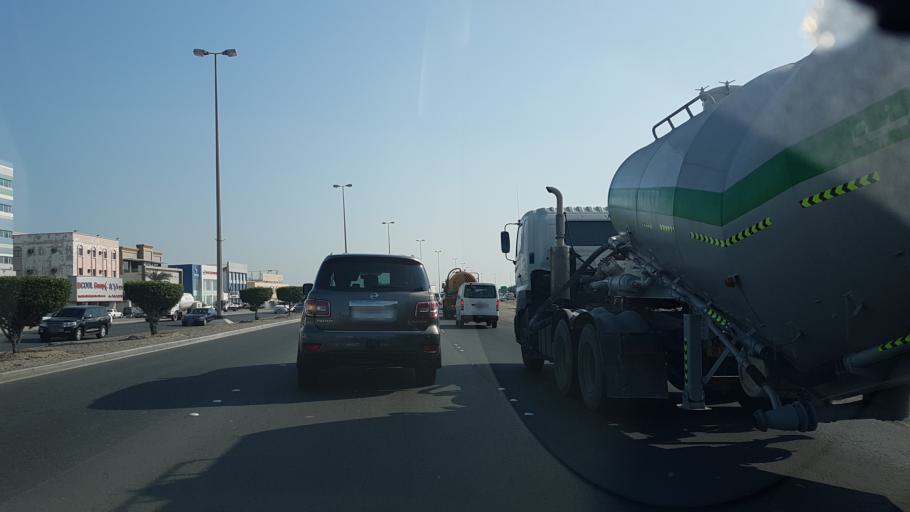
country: BH
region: Northern
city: Sitrah
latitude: 26.1504
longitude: 50.6176
